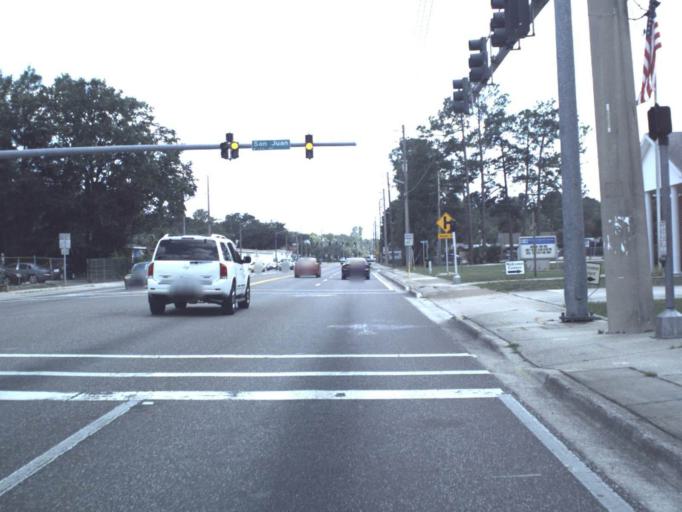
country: US
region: Florida
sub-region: Clay County
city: Bellair-Meadowbrook Terrace
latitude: 30.2822
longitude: -81.7553
